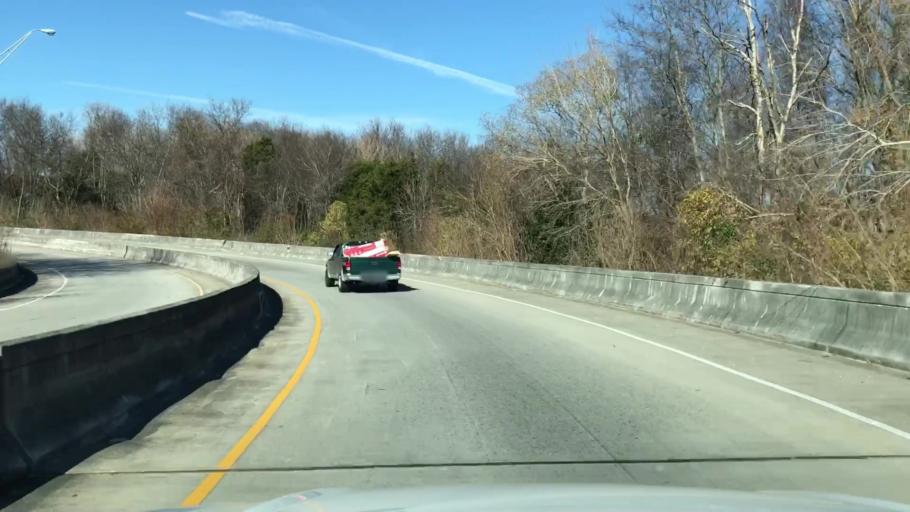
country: US
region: South Carolina
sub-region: Charleston County
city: Charleston
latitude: 32.7752
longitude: -79.9569
